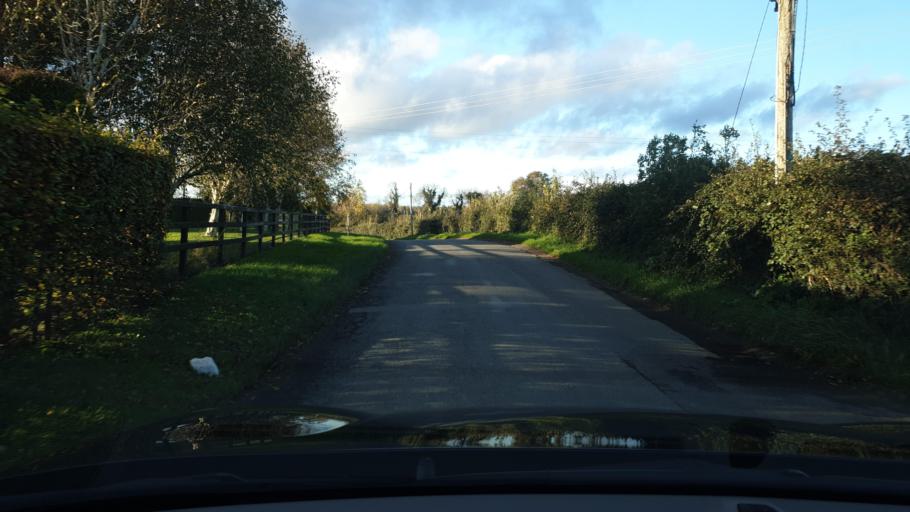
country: IE
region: Leinster
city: Balrothery
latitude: 53.5931
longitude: -6.2092
